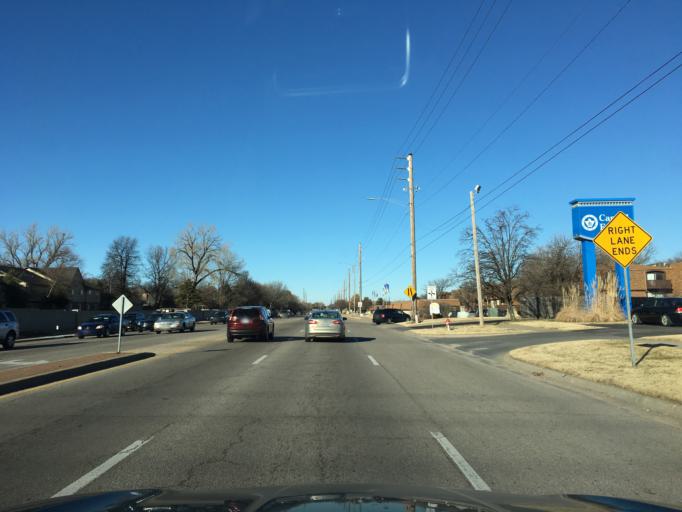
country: US
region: Kansas
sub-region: Sedgwick County
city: Bellaire
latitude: 37.6867
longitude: -97.2444
